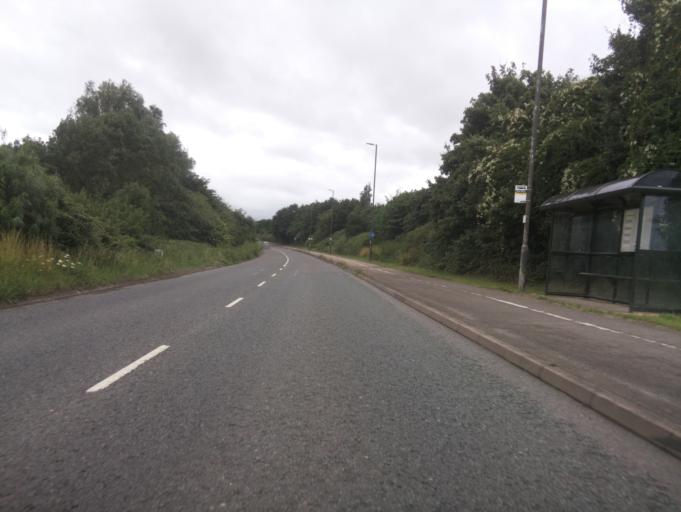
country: GB
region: England
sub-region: Gloucestershire
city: Tewkesbury
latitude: 51.9788
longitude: -2.1500
